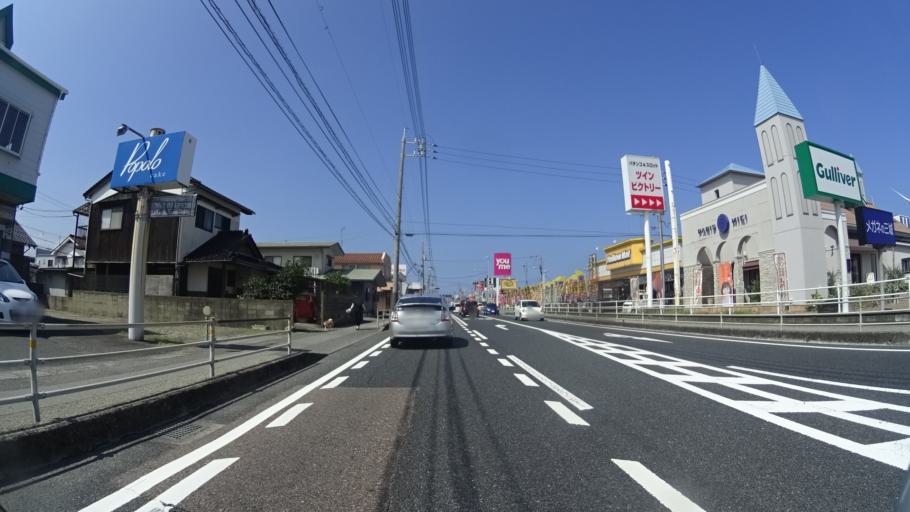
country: JP
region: Shimane
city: Masuda
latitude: 34.6895
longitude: 131.8180
